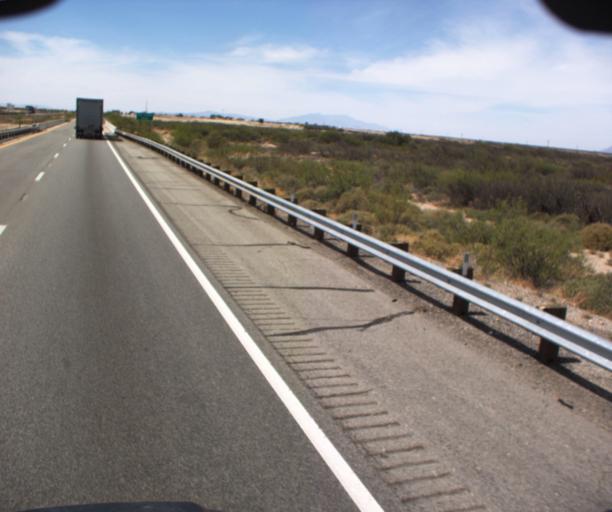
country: US
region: New Mexico
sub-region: Hidalgo County
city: Lordsburg
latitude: 32.2581
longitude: -109.2046
